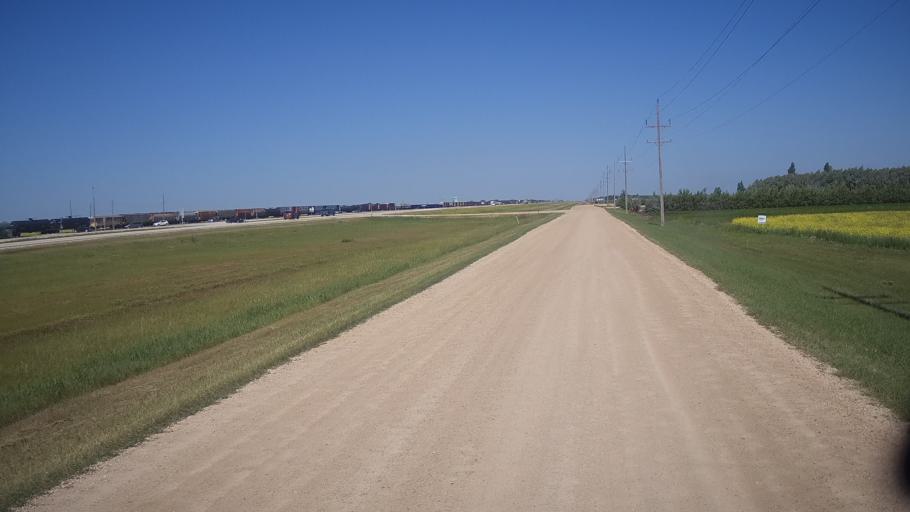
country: CA
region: Manitoba
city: Niverville
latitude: 49.7721
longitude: -96.8180
